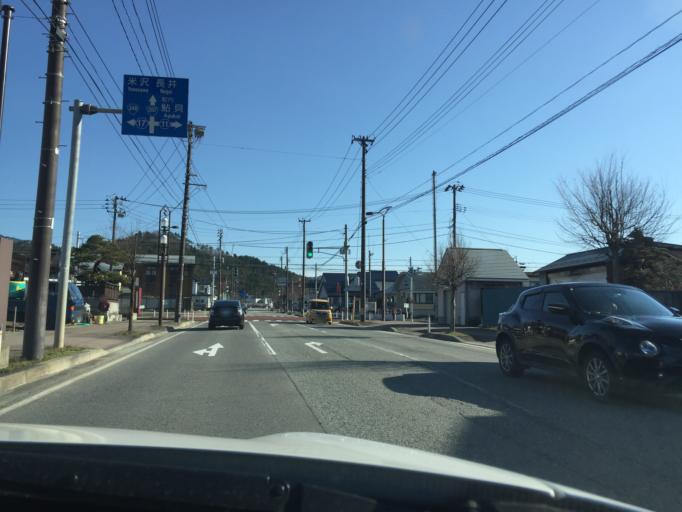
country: JP
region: Yamagata
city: Nagai
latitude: 38.1847
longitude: 140.1016
